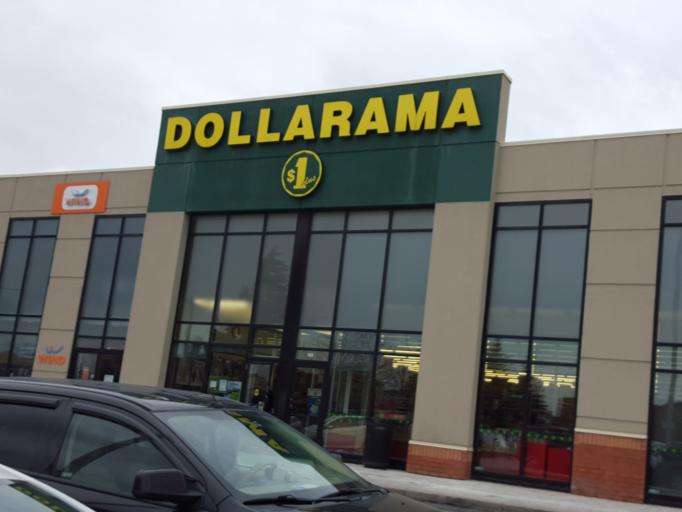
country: CA
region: Ontario
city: Concord
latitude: 43.7868
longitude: -79.5458
